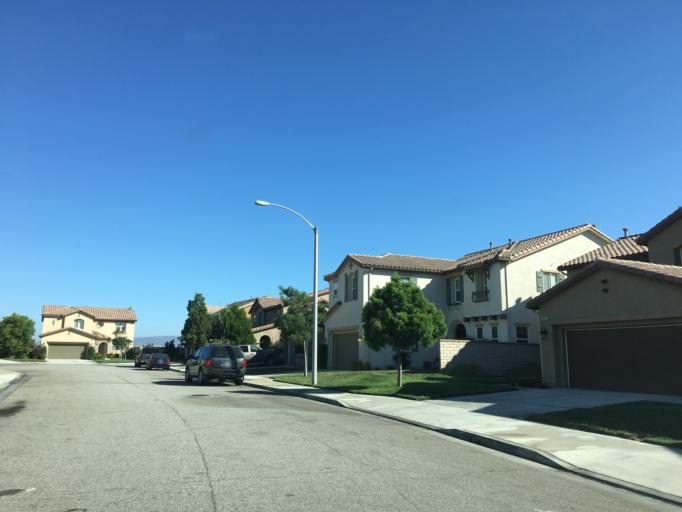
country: US
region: California
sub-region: Los Angeles County
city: Santa Clarita
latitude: 34.4403
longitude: -118.4931
